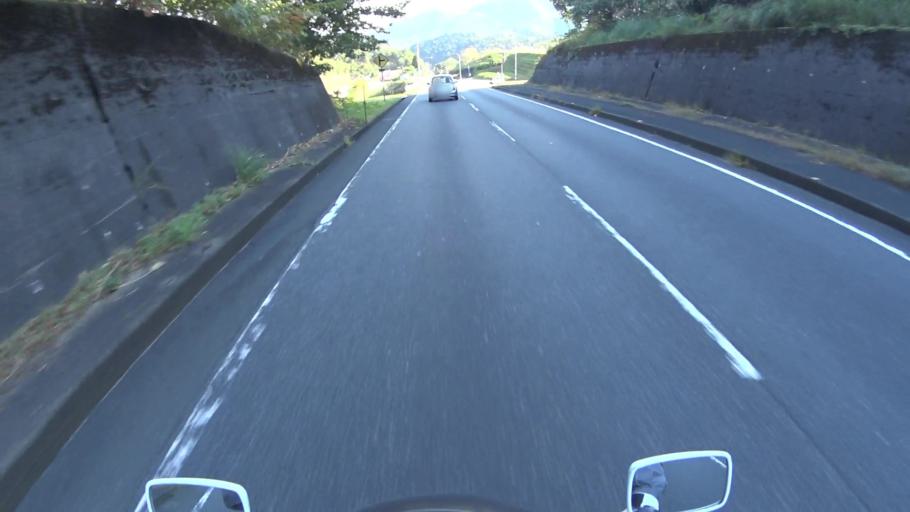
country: JP
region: Kyoto
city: Fukuchiyama
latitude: 35.3781
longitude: 135.0984
